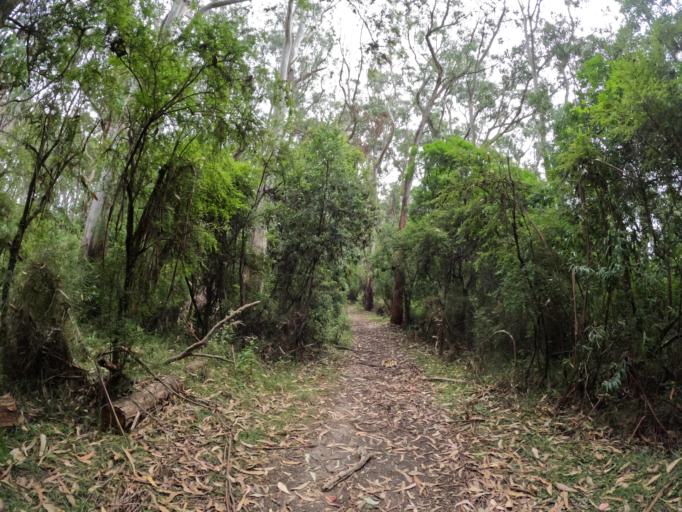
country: AU
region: Victoria
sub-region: Colac-Otway
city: Apollo Bay
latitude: -38.7927
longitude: 143.6170
